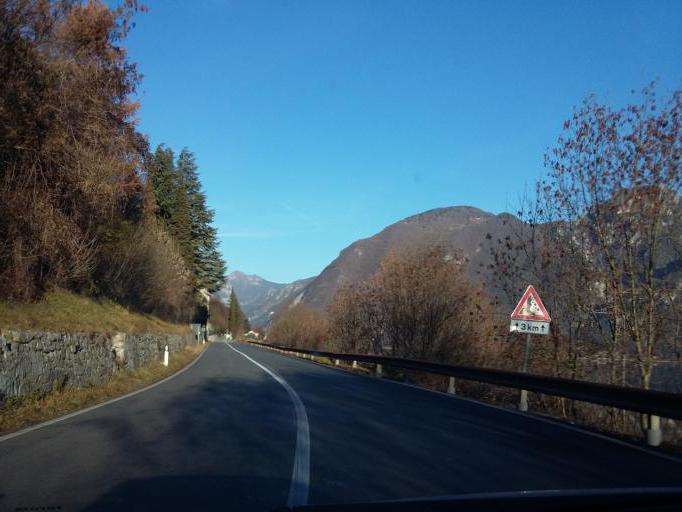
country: IT
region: Lombardy
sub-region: Provincia di Brescia
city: Anfo
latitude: 45.7700
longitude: 10.4978
